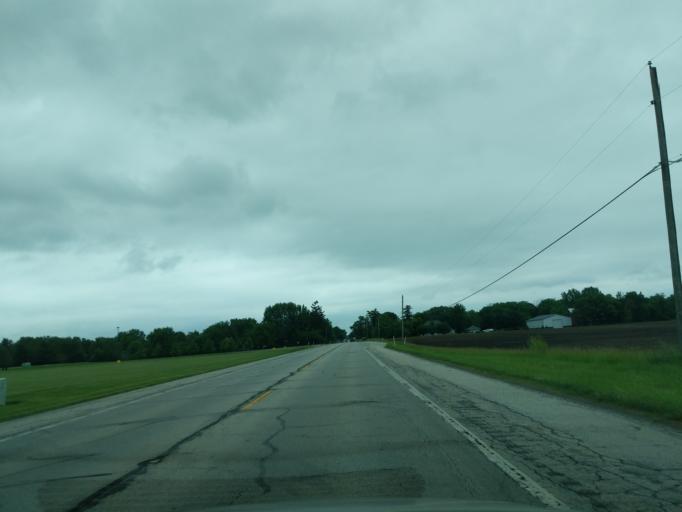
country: US
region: Indiana
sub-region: Hamilton County
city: Arcadia
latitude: 40.1652
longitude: -86.0132
